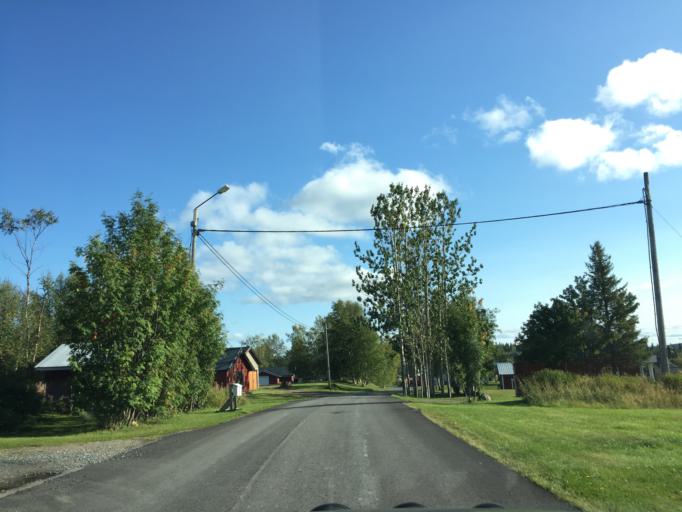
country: SE
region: Norrbotten
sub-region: Gallivare Kommun
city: Malmberget
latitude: 67.6485
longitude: 21.0594
